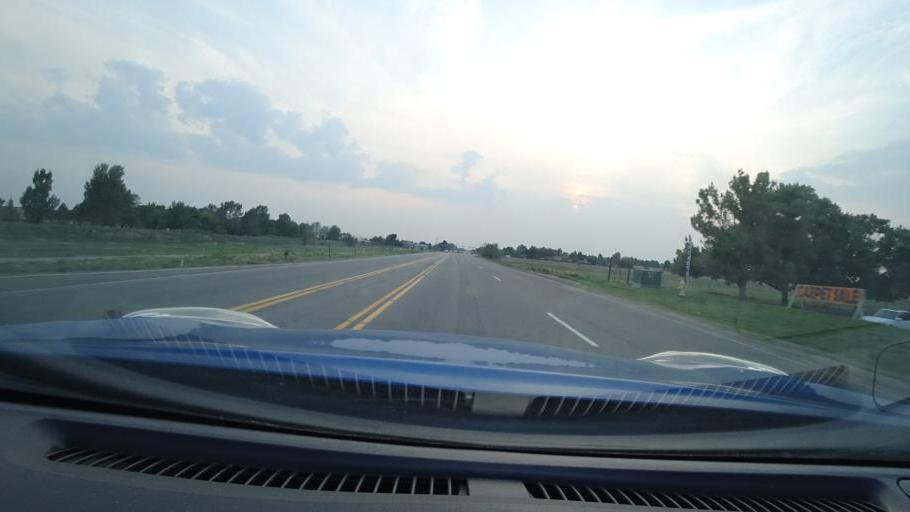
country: US
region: Colorado
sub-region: Adams County
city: Aurora
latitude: 39.7256
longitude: -104.7870
